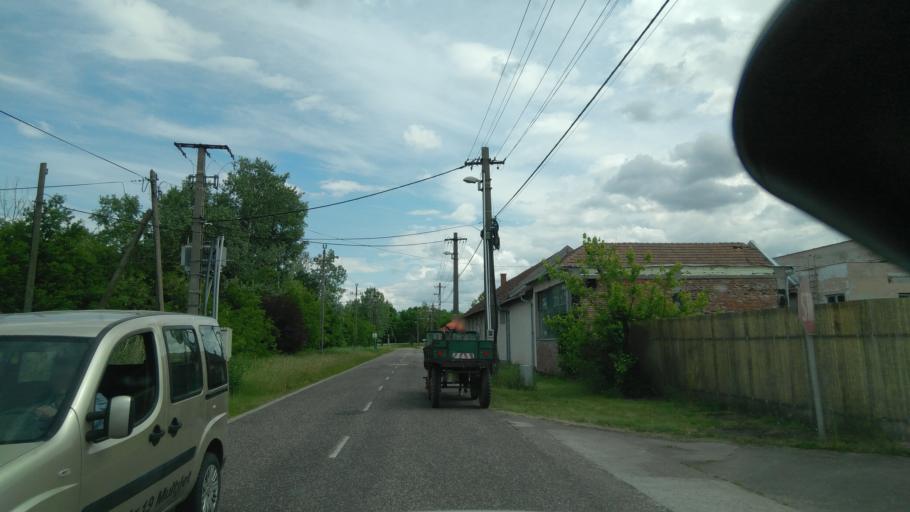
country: HU
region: Bekes
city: Oroshaza
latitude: 46.5727
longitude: 20.6208
